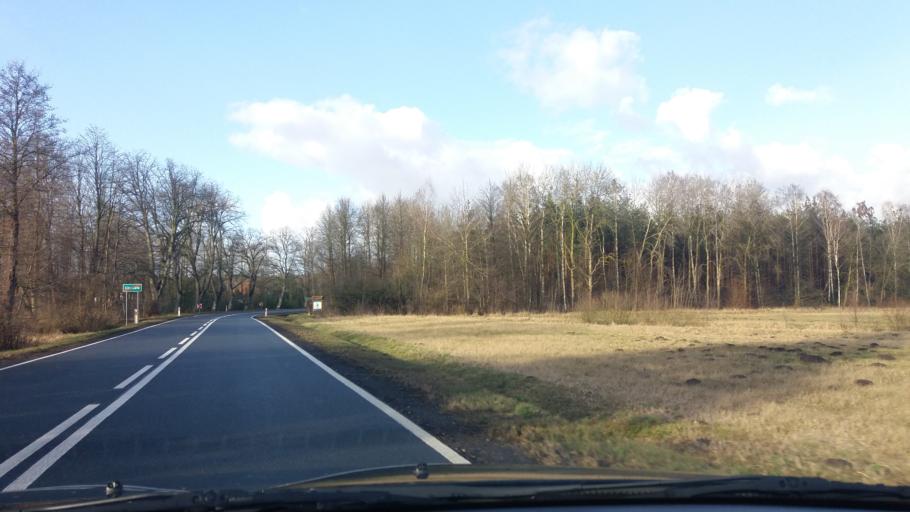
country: PL
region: Masovian Voivodeship
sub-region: Powiat przasnyski
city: Chorzele
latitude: 53.2788
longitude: 20.8987
